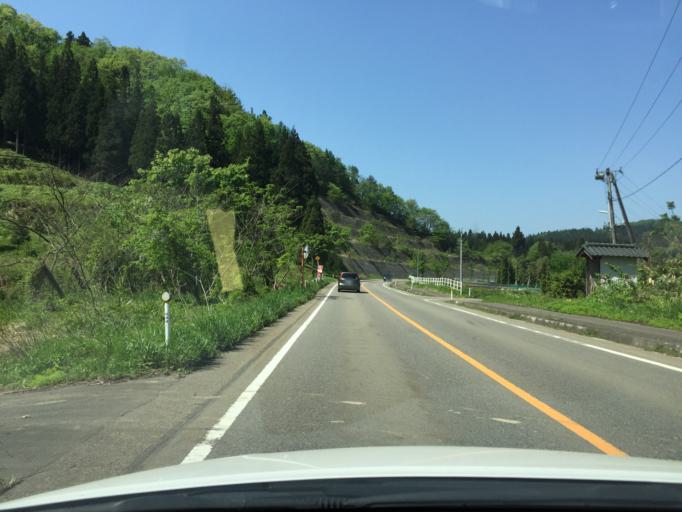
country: JP
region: Niigata
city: Kamo
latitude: 37.6341
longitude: 139.1047
